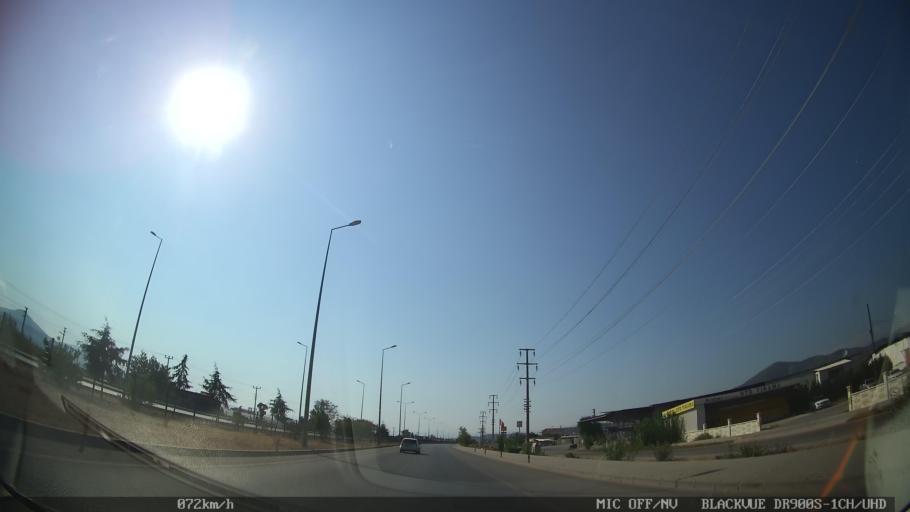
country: TR
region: Mugla
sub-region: Fethiye
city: Fethiye
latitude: 36.6554
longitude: 29.1641
